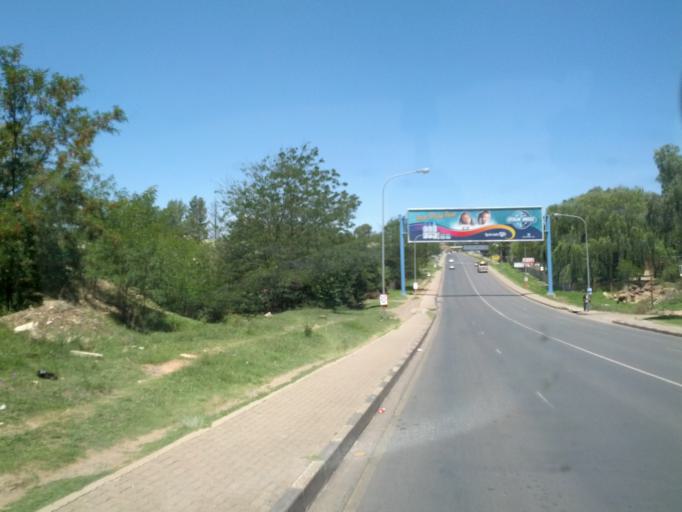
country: LS
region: Maseru
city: Maseru
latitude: -29.3014
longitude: 27.4818
